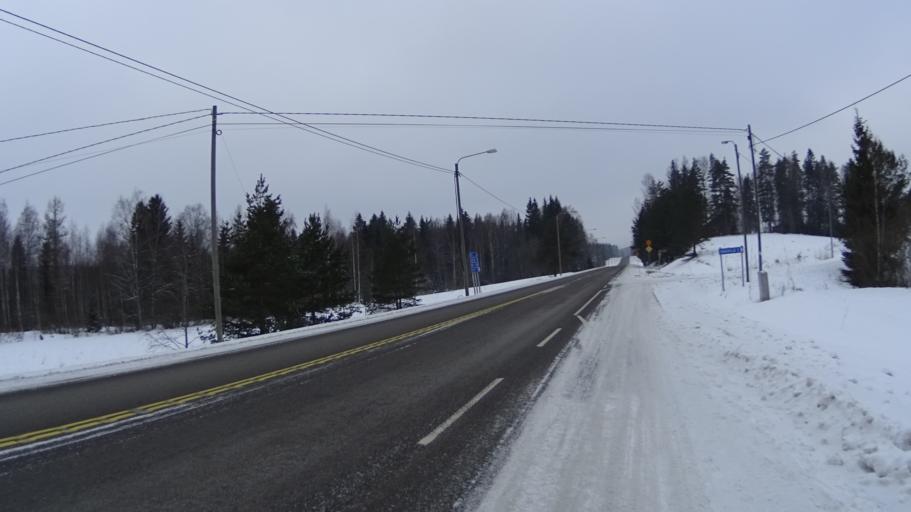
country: FI
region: Uusimaa
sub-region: Helsinki
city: Saukkola
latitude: 60.3742
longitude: 24.1066
